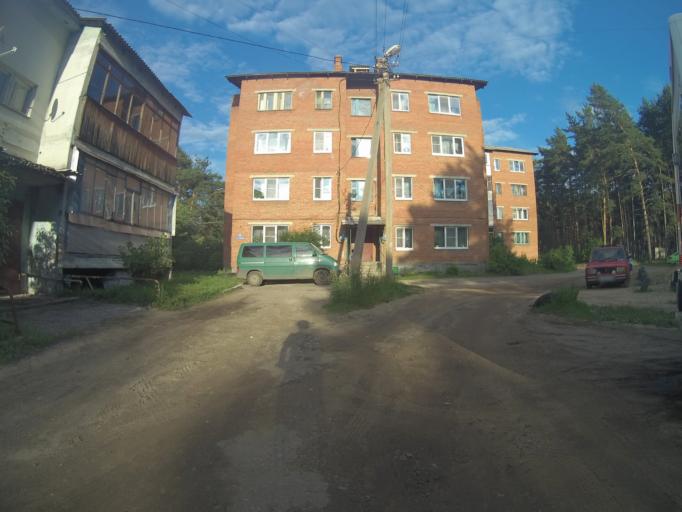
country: RU
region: Vladimir
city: Kommunar
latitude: 56.1224
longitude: 40.4628
